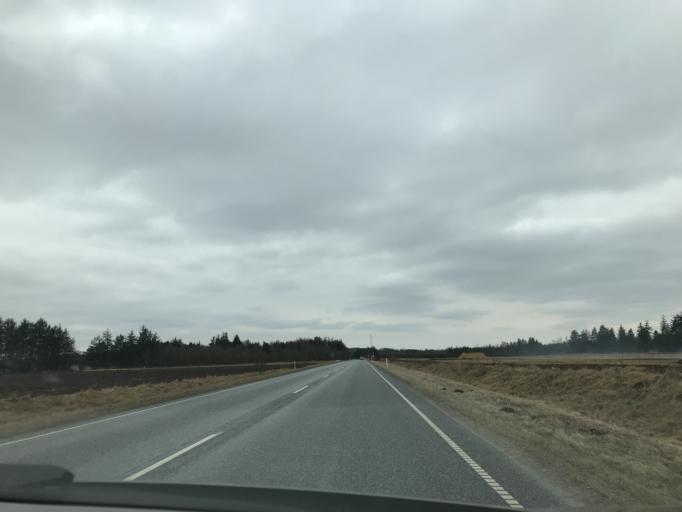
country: DK
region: South Denmark
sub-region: Varde Kommune
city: Olgod
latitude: 55.8475
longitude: 8.7283
